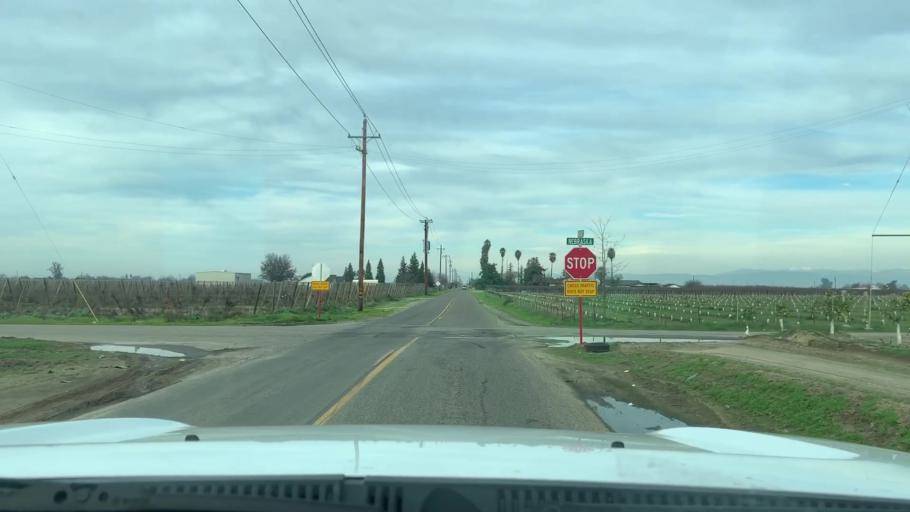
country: US
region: California
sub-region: Fresno County
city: Selma
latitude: 36.5612
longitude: -119.5750
